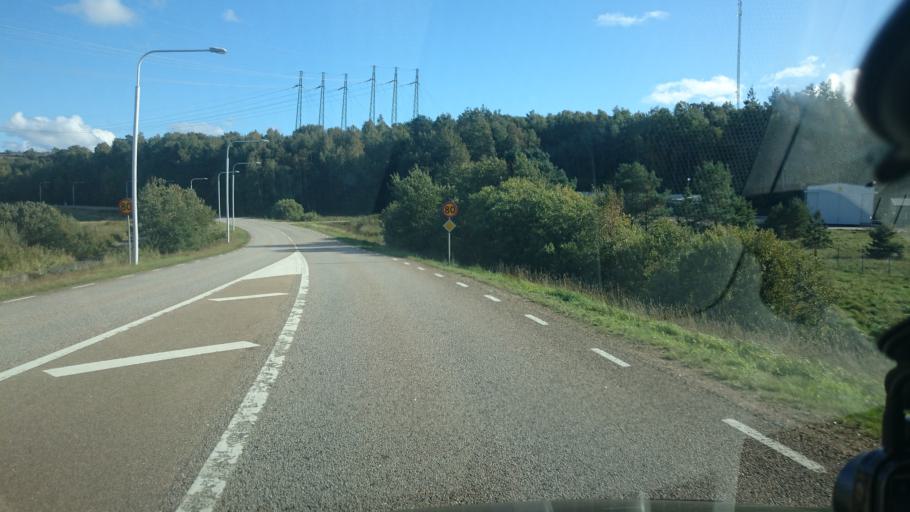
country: SE
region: Vaestra Goetaland
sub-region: Lysekils Kommun
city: Lysekil
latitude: 58.3364
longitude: 11.4219
